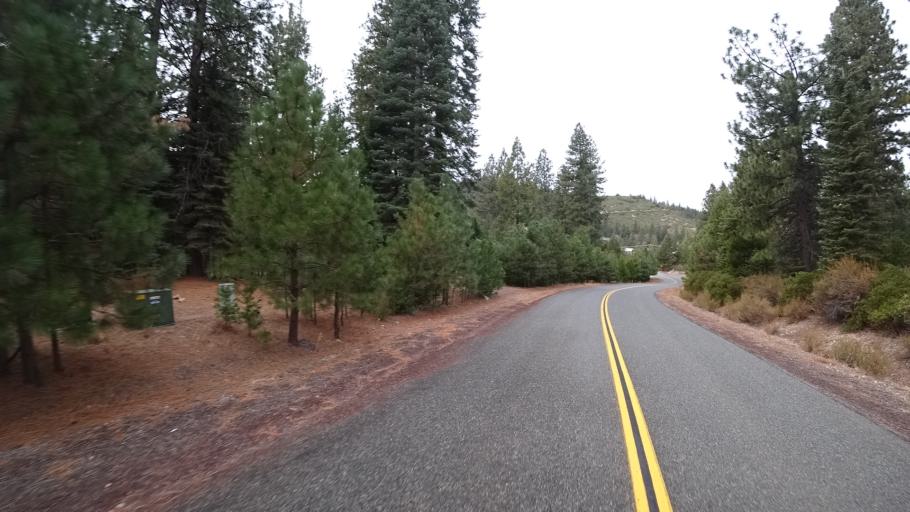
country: US
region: California
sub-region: Siskiyou County
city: Weed
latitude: 41.4094
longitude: -122.3756
